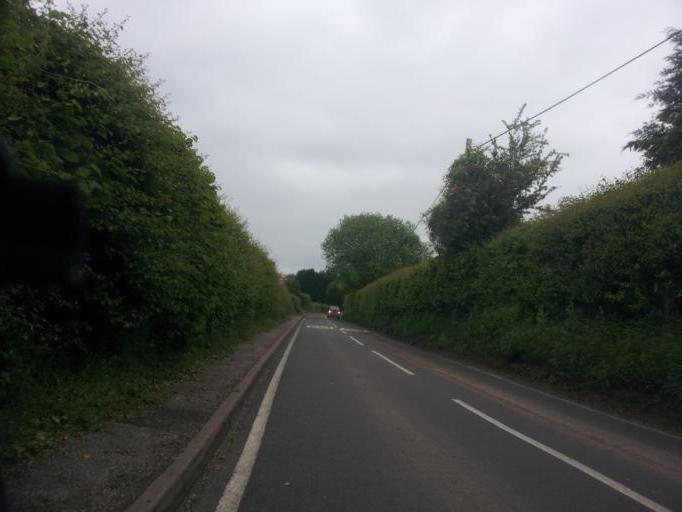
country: GB
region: England
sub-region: Kent
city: Maidstone
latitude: 51.2539
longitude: 0.4722
